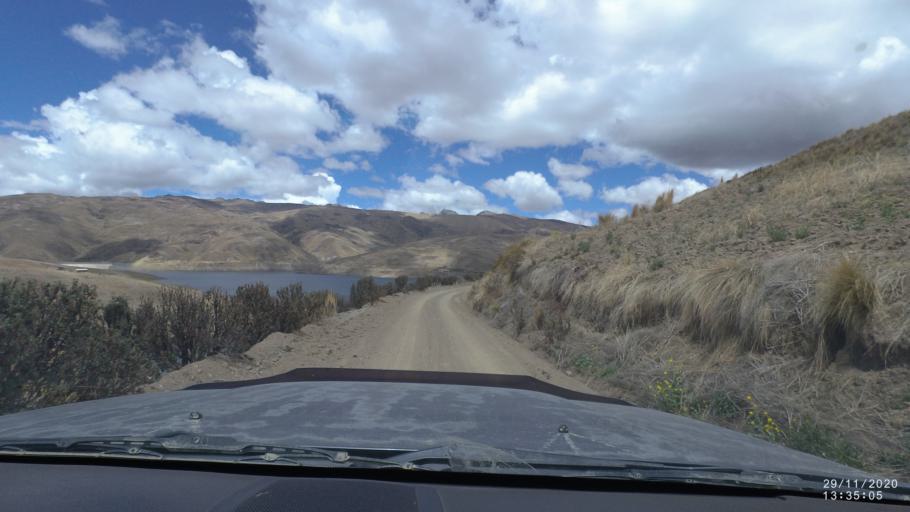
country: BO
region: Cochabamba
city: Cochabamba
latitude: -17.1127
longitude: -66.3338
